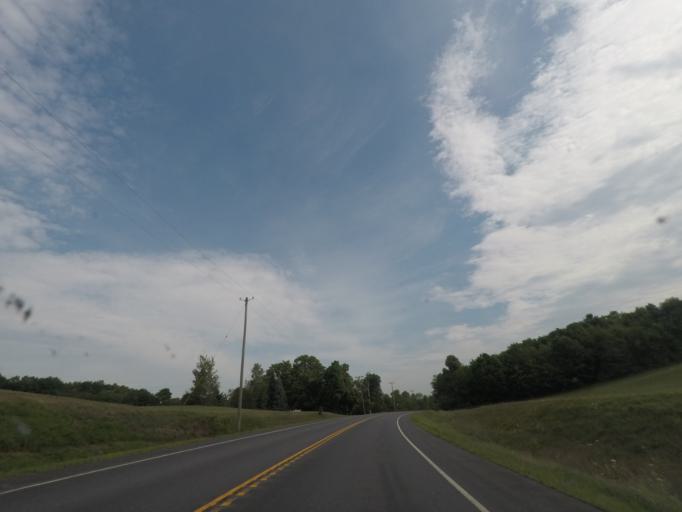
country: US
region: New York
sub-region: Rensselaer County
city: Poestenkill
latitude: 42.6828
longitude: -73.5681
